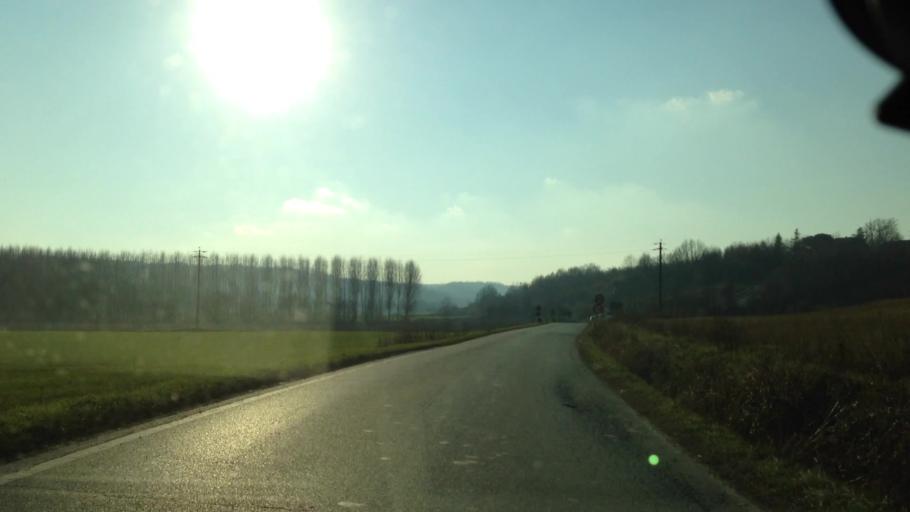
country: IT
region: Piedmont
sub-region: Provincia di Alessandria
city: Masio
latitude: 44.8462
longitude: 8.3968
